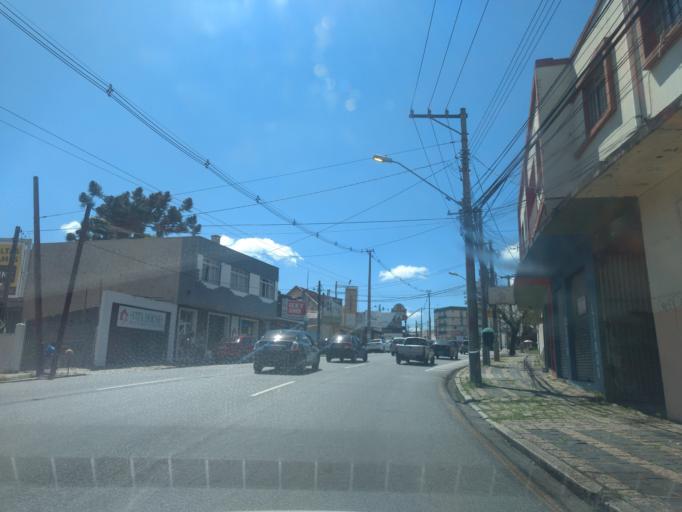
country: BR
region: Parana
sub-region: Curitiba
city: Curitiba
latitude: -25.4052
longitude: -49.2467
